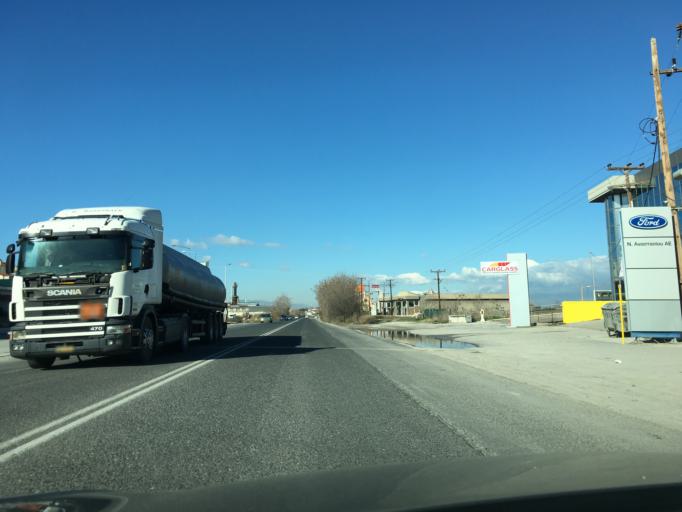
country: GR
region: Thessaly
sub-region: Nomos Larisis
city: Larisa
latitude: 39.6119
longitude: 22.4350
